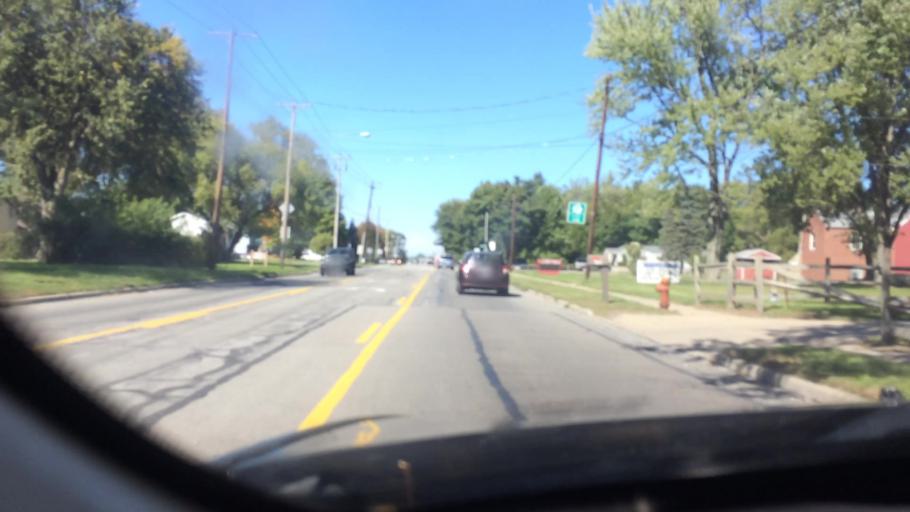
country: US
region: Ohio
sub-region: Lucas County
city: Ottawa Hills
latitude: 41.6678
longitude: -83.6824
